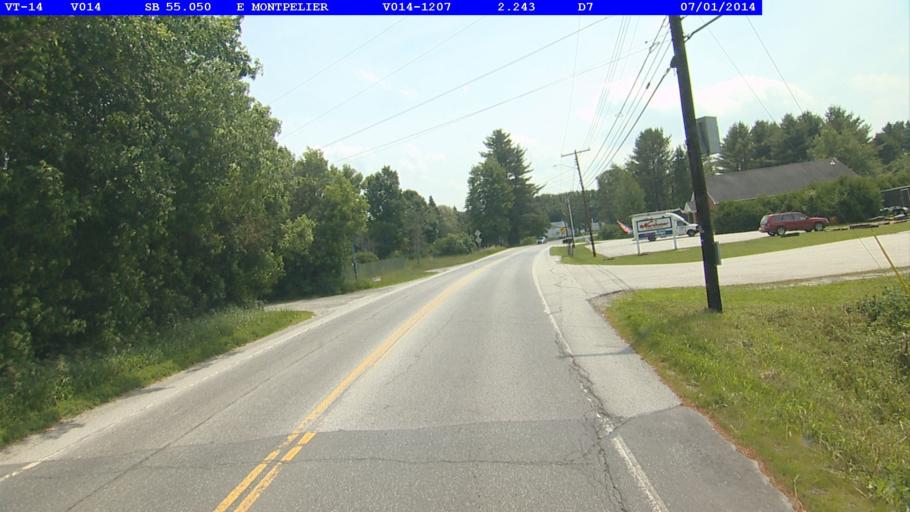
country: US
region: Vermont
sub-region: Washington County
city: Barre
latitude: 44.2656
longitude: -72.4864
